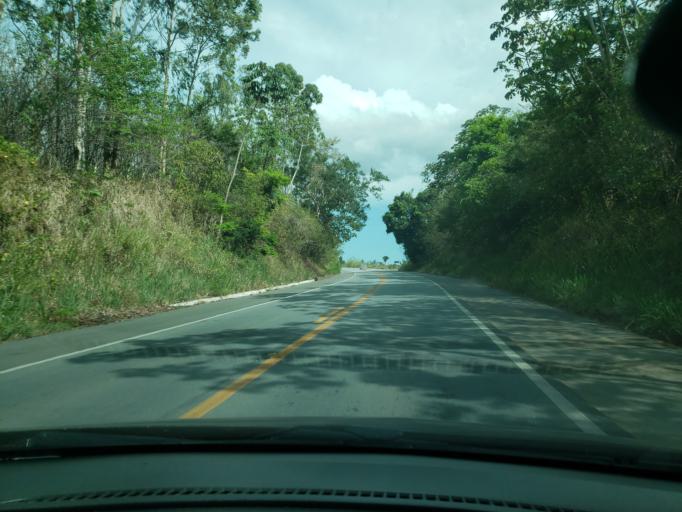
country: BR
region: Alagoas
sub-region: Murici
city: Murici
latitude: -9.3253
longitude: -35.9230
